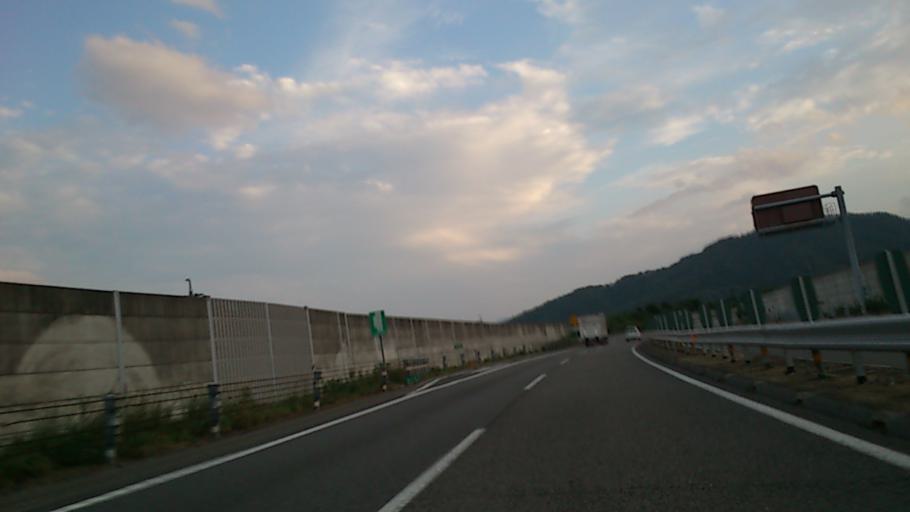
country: JP
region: Nagano
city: Iida
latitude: 35.4944
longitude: 137.7932
